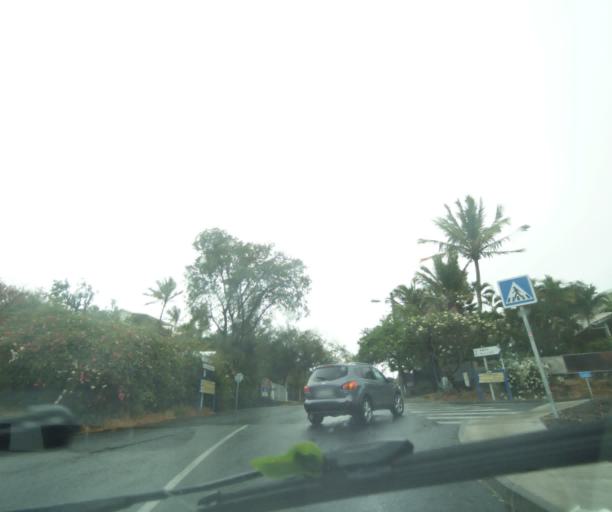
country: RE
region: Reunion
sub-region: Reunion
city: Saint-Paul
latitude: -21.0279
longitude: 55.2289
